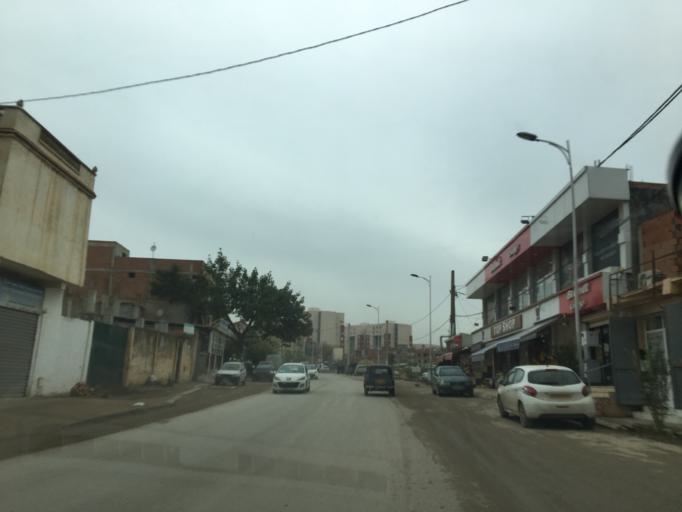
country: DZ
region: Alger
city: Ain Taya
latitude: 36.7737
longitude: 3.2516
